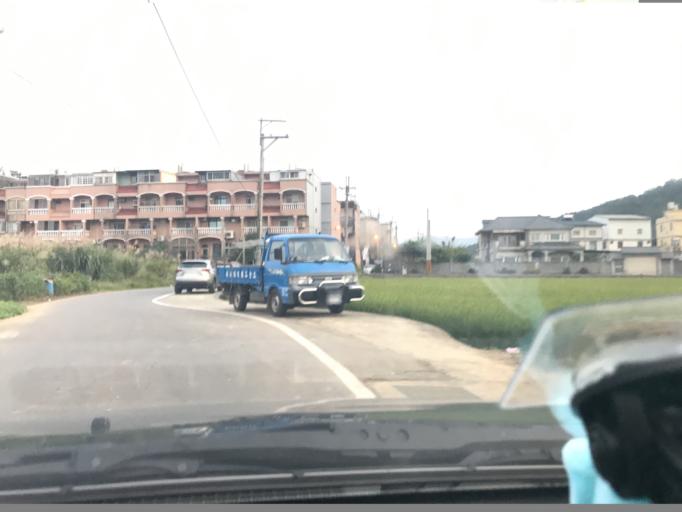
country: TW
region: Taiwan
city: Daxi
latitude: 24.8509
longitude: 121.2083
